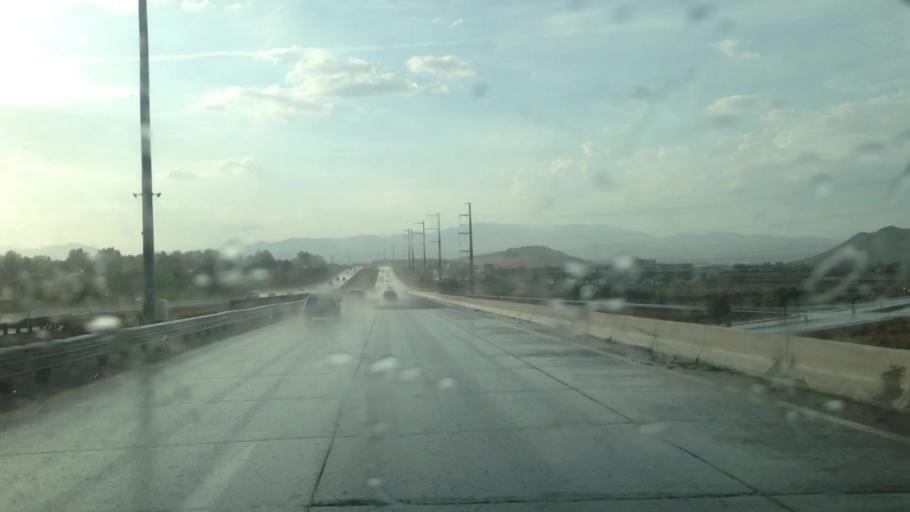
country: US
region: Nevada
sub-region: Washoe County
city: Golden Valley
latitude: 39.5993
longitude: -119.8365
